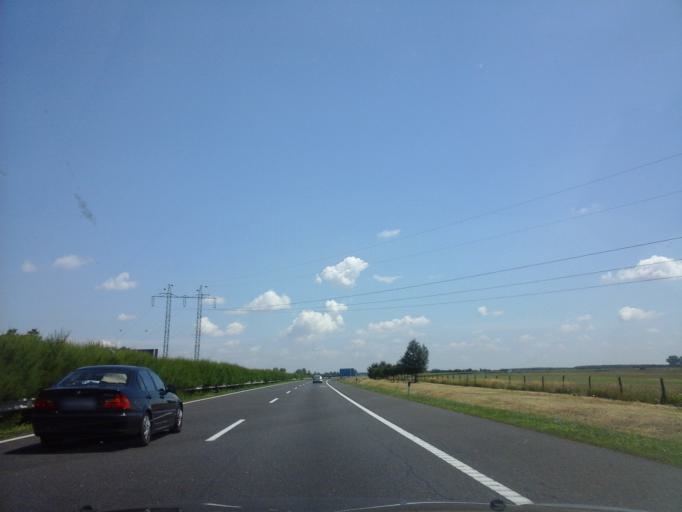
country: HU
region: Borsod-Abauj-Zemplen
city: Emod
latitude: 47.8835
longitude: 20.8454
